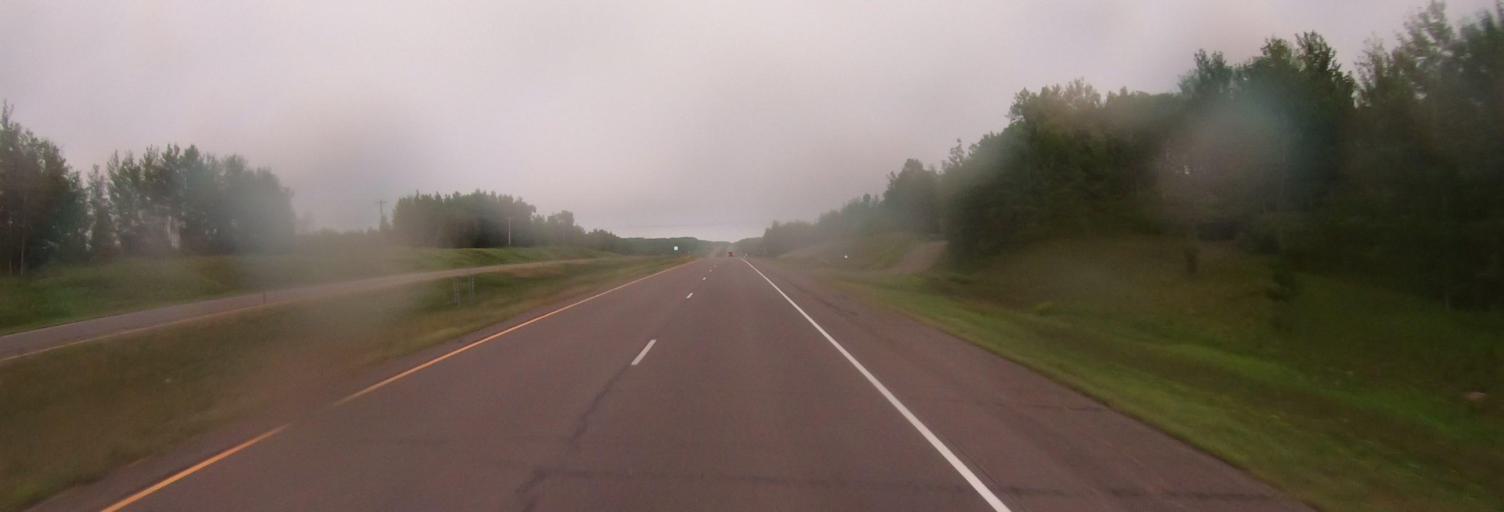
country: US
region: Minnesota
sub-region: Carlton County
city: Cloquet
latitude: 46.9177
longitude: -92.4702
